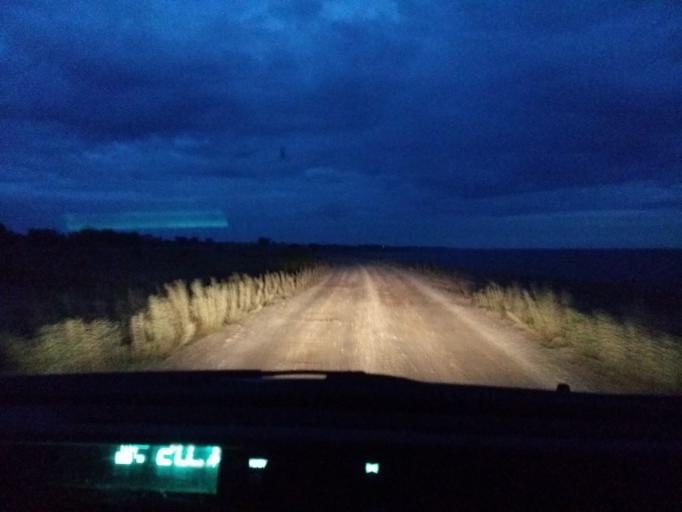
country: SE
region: Kalmar
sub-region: Borgholms Kommun
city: Borgholm
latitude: 57.1187
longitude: 16.8979
